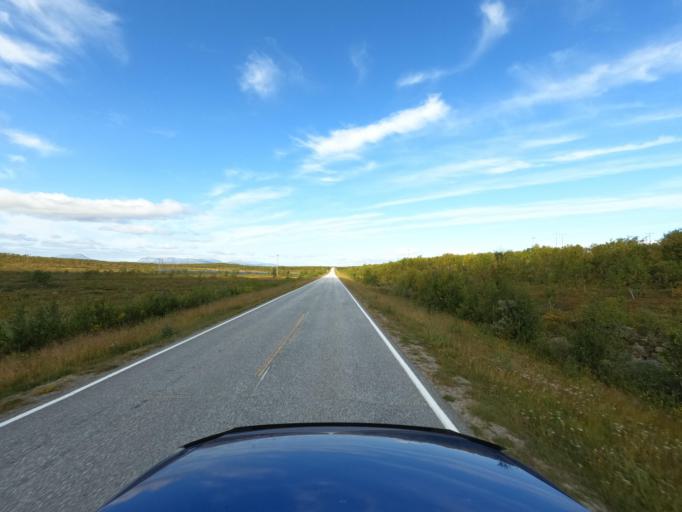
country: NO
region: Finnmark Fylke
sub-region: Karasjok
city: Karasjohka
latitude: 69.7015
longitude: 25.2543
